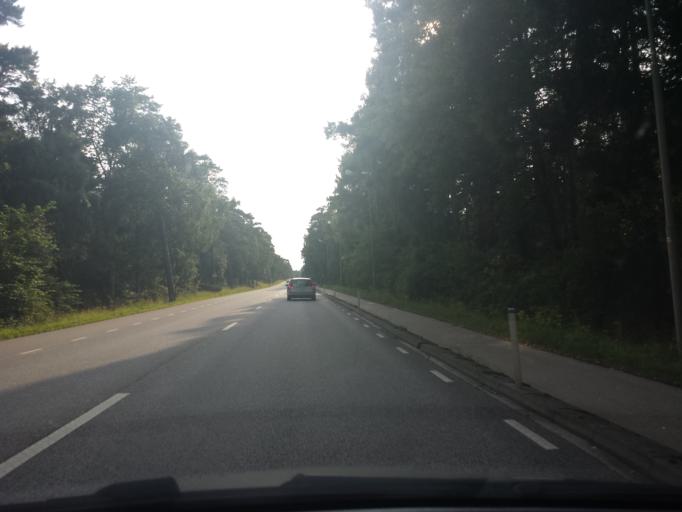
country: SE
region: Skane
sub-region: Ystads Kommun
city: Ystad
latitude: 55.4347
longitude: 13.8782
